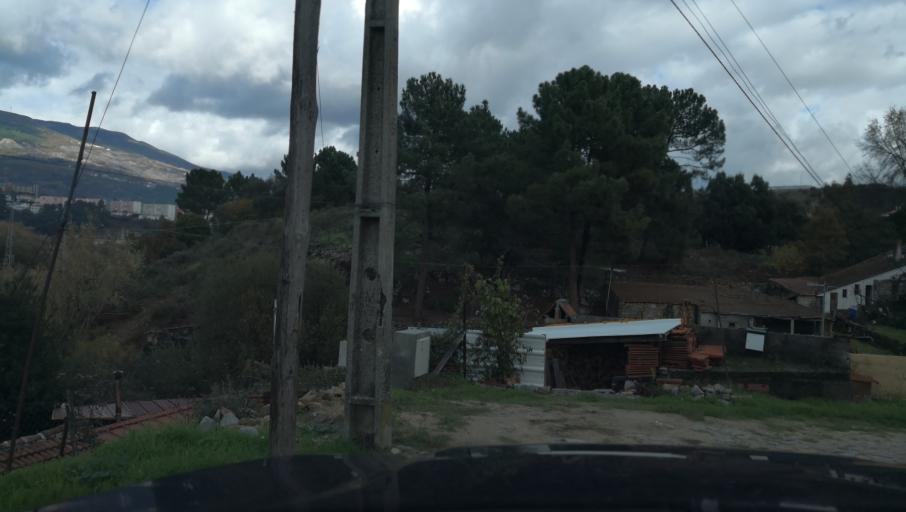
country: PT
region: Vila Real
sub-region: Vila Real
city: Vila Real
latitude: 41.2983
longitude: -7.7577
